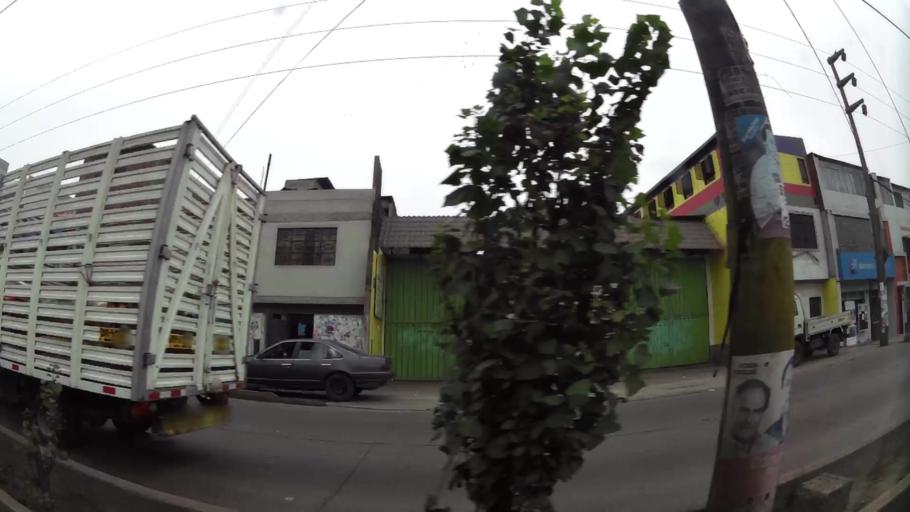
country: PE
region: Lima
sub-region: Lima
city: Vitarte
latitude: -12.0241
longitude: -76.9142
